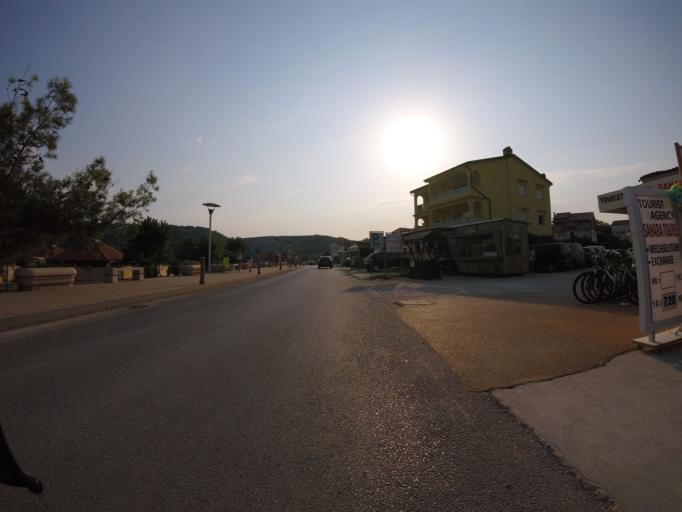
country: HR
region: Primorsko-Goranska
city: Lopar
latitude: 44.8255
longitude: 14.7417
